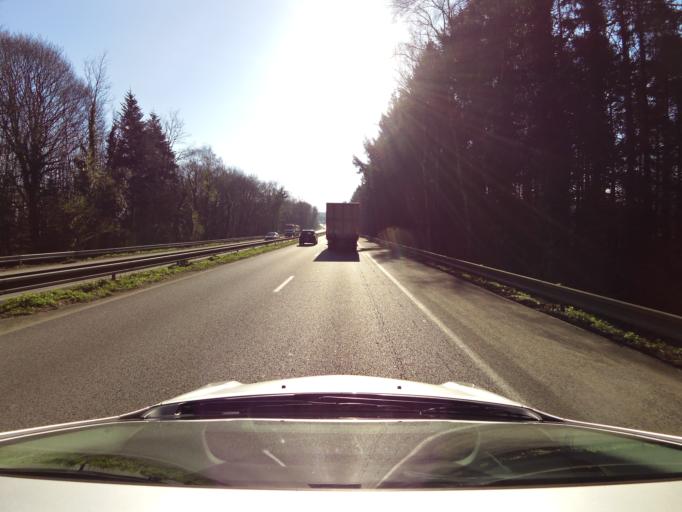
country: FR
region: Brittany
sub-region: Departement du Morbihan
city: Hennebont
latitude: 47.7889
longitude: -3.2885
